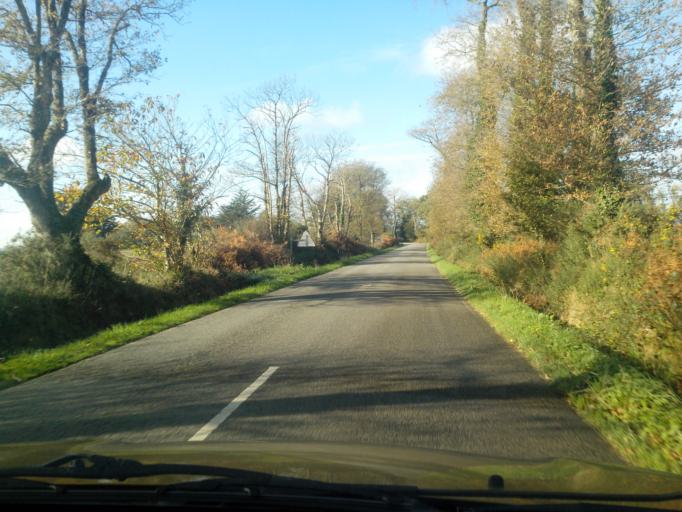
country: FR
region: Brittany
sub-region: Departement du Morbihan
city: Molac
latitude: 47.7309
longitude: -2.4264
